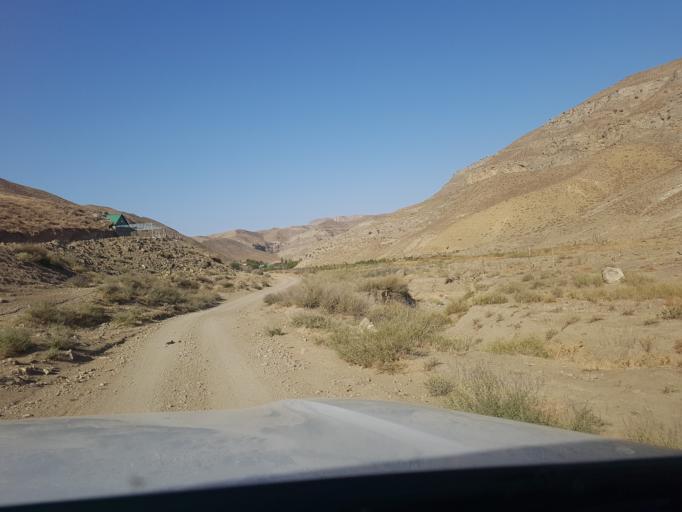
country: TM
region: Balkan
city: Magtymguly
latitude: 38.3007
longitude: 56.7580
